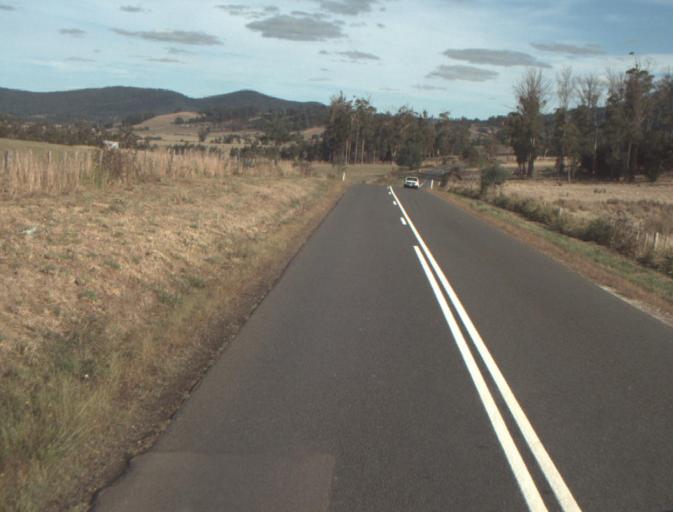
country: AU
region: Tasmania
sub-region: Launceston
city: Mayfield
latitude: -41.2155
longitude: 147.1214
